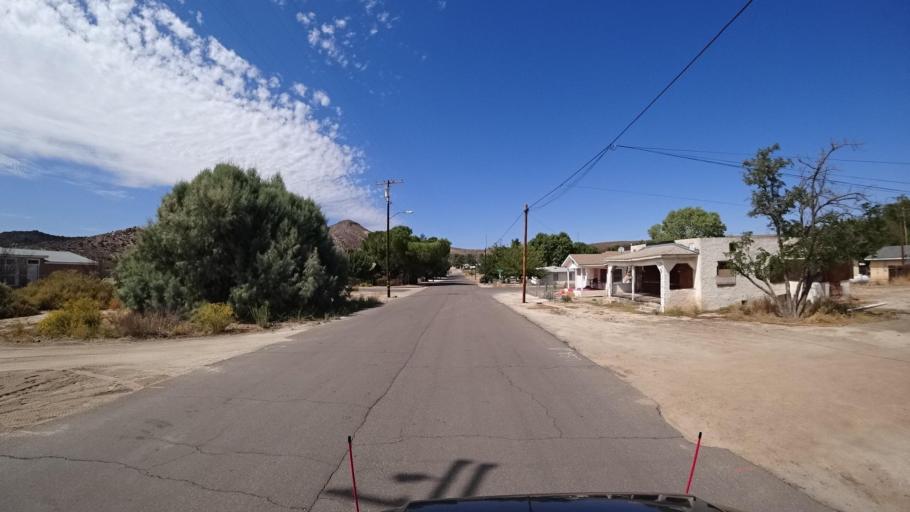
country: MX
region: Baja California
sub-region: Tecate
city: Cereso del Hongo
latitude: 32.6181
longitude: -116.1901
